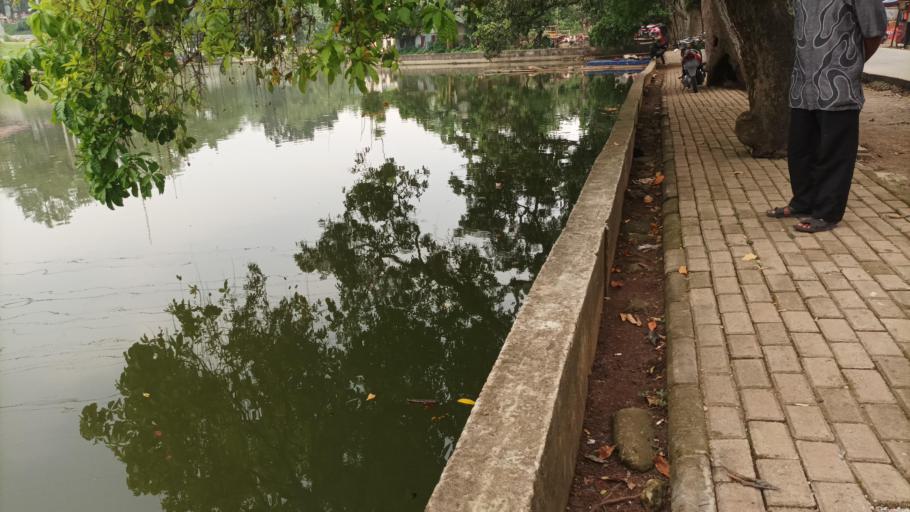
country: ID
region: West Java
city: Depok
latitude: -6.4155
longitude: 106.8438
